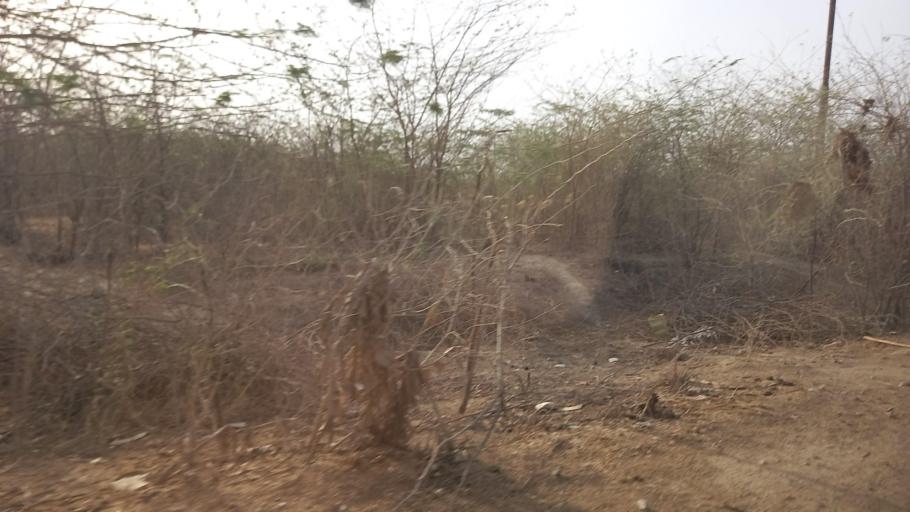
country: PK
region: Sindh
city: Malir Cantonment
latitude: 25.1137
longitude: 67.1915
